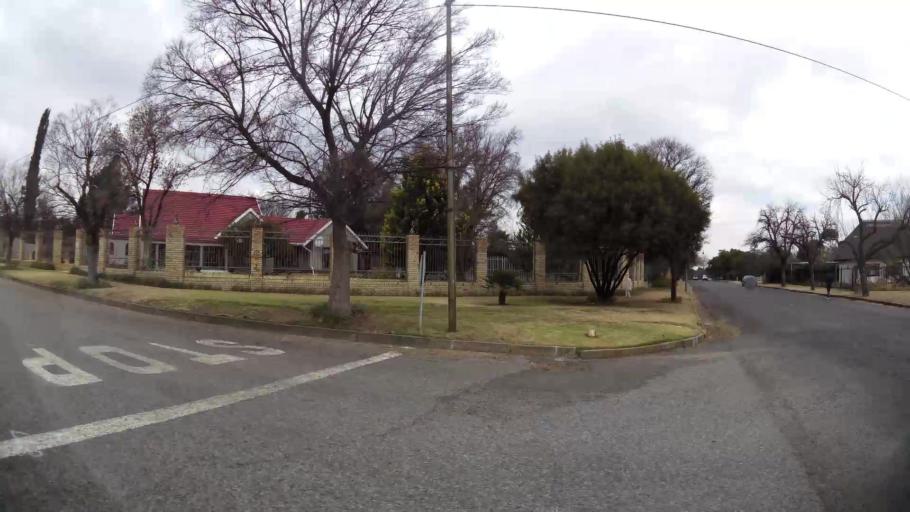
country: ZA
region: Orange Free State
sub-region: Fezile Dabi District Municipality
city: Kroonstad
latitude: -27.6757
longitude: 27.2424
